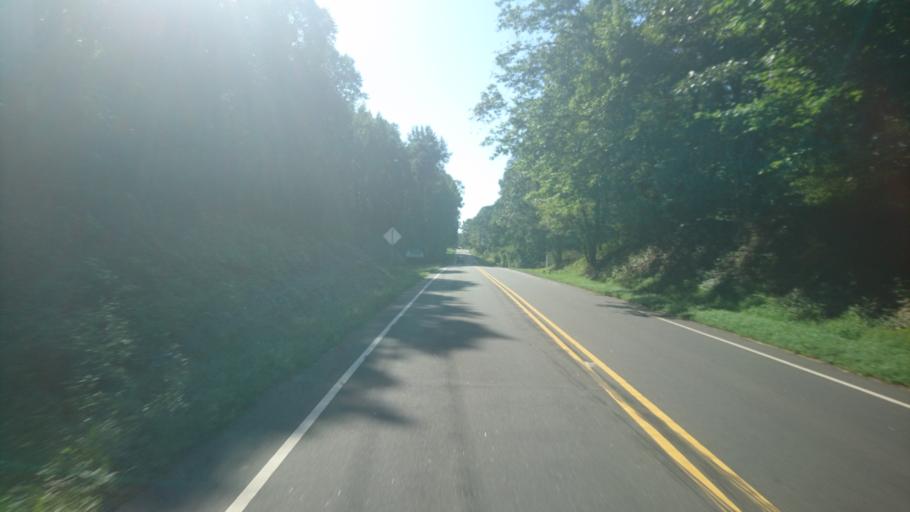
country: US
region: North Carolina
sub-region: Orange County
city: Hillsborough
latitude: 36.0123
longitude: -79.0705
